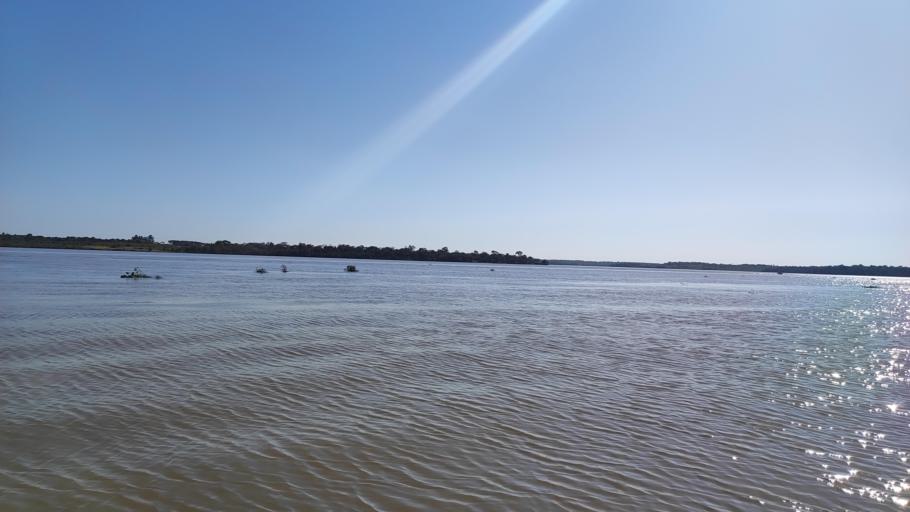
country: PY
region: Itapua
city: San Juan del Parana
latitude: -27.3379
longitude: -56.0061
